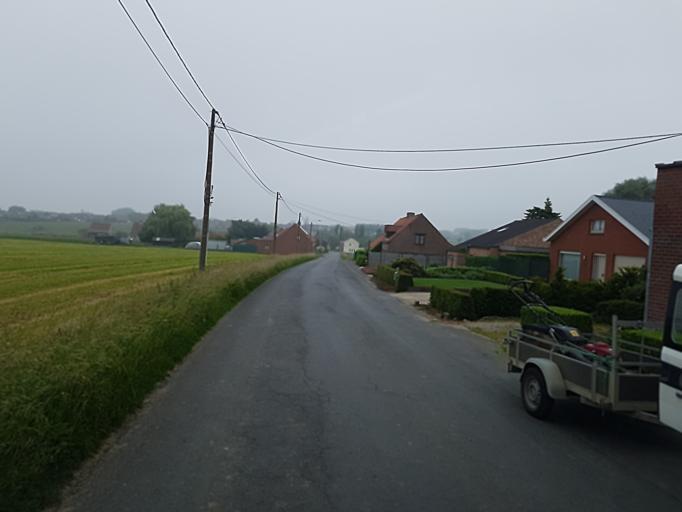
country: BE
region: Flanders
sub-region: Provincie West-Vlaanderen
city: Zonnebeke
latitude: 50.8629
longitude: 2.9782
